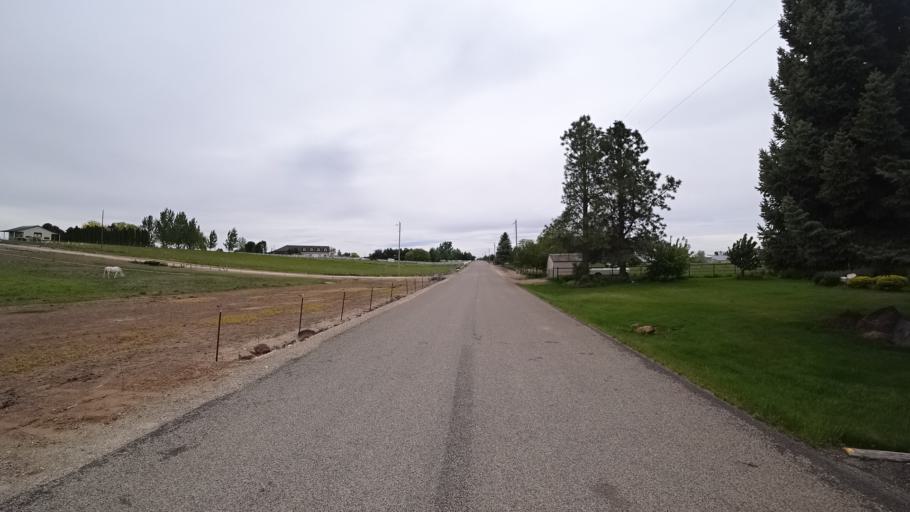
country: US
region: Idaho
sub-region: Ada County
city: Kuna
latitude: 43.5023
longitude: -116.3394
